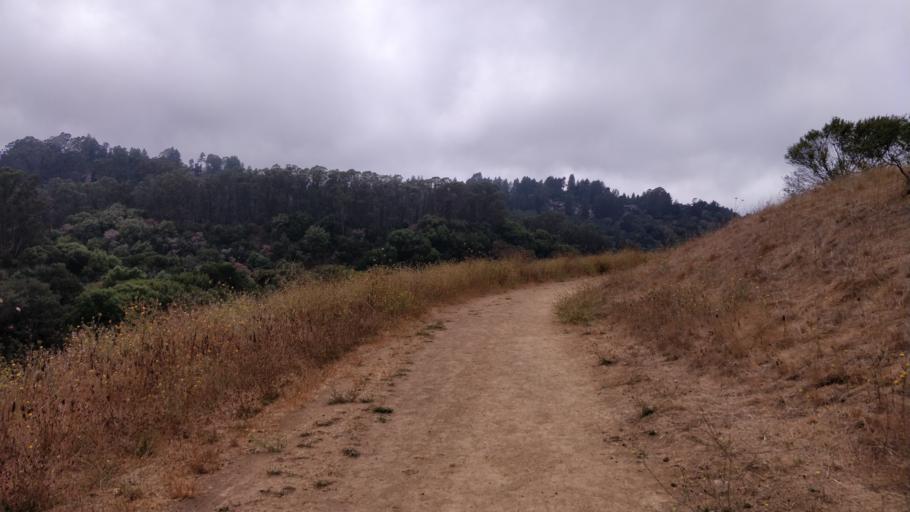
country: US
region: California
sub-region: Contra Costa County
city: Kensington
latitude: 37.9045
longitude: -122.2499
